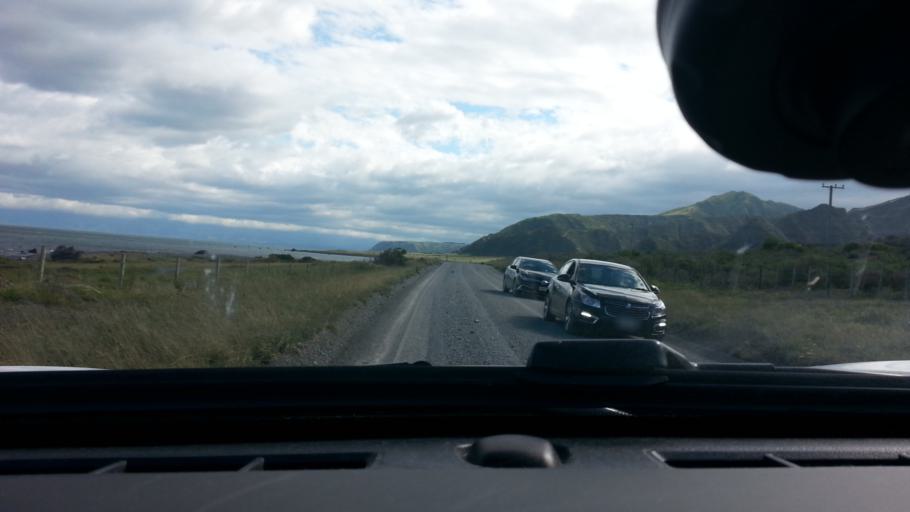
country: NZ
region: Wellington
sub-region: South Wairarapa District
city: Waipawa
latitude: -41.5936
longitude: 175.2338
